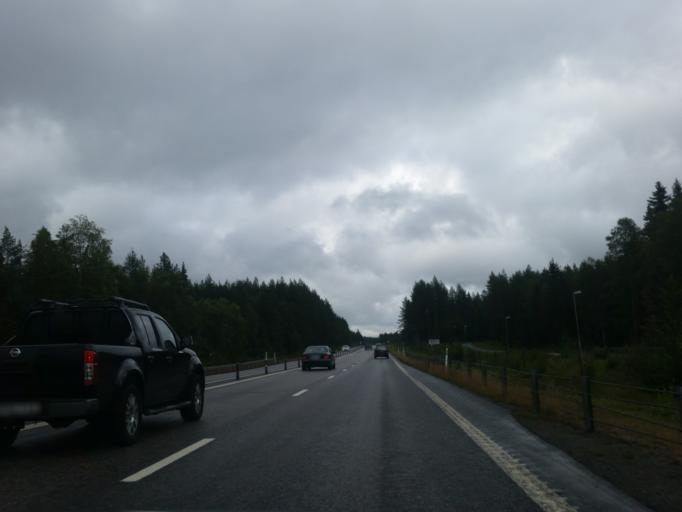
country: SE
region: Vaesterbotten
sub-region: Umea Kommun
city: Taftea
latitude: 63.8650
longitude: 20.4284
